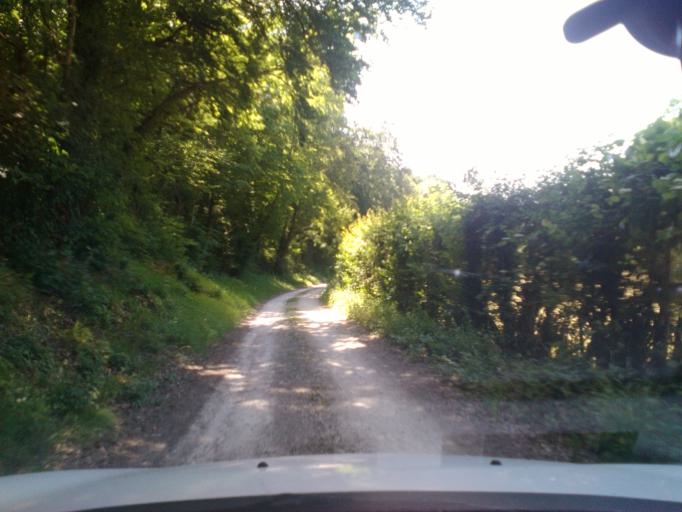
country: FR
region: Lorraine
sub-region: Departement des Vosges
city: Liffol-le-Grand
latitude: 48.3114
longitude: 5.3989
